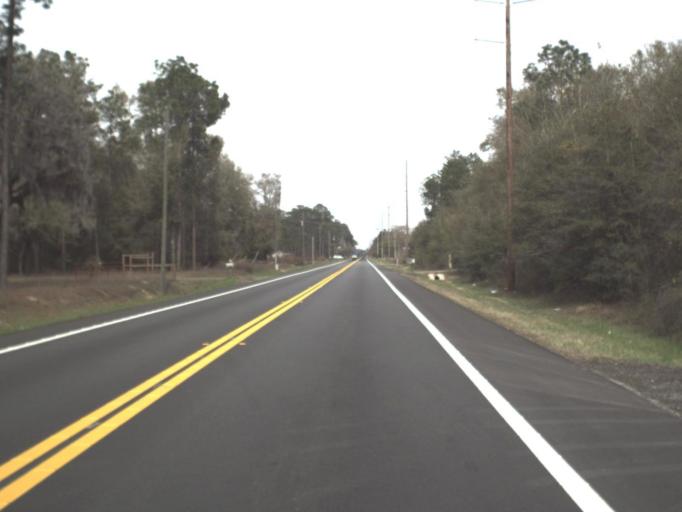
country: US
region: Florida
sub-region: Gadsden County
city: Midway
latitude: 30.4168
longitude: -84.5476
